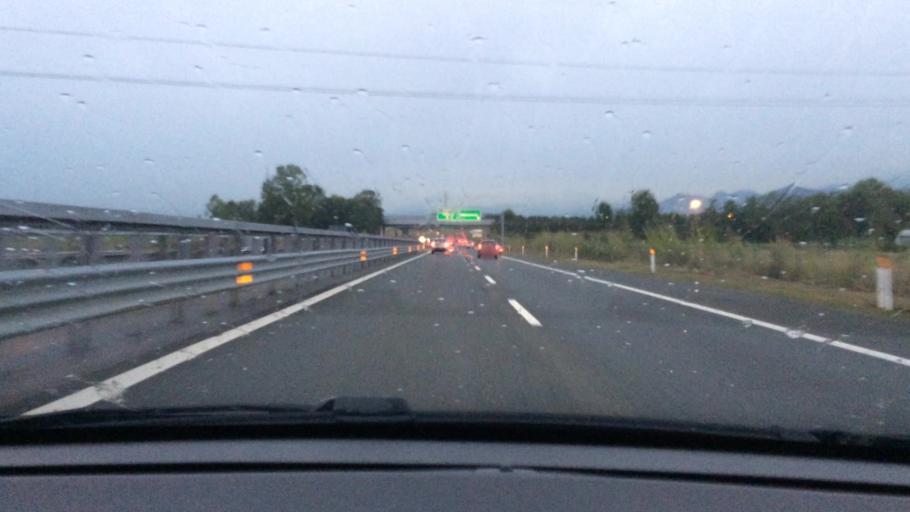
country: IT
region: Piedmont
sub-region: Provincia di Torino
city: Borgo Melano
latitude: 45.0092
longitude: 7.5748
